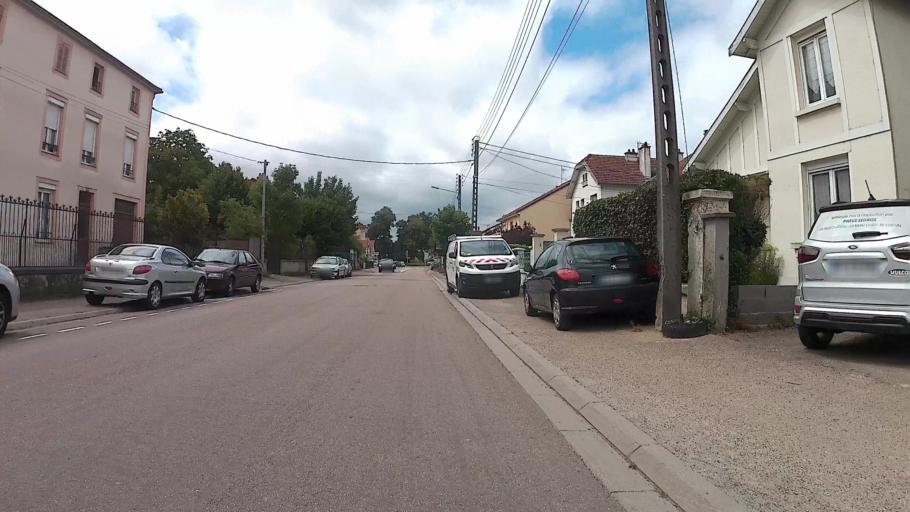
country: FR
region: Lorraine
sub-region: Departement de la Meuse
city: Verdun
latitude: 49.1590
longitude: 5.3970
